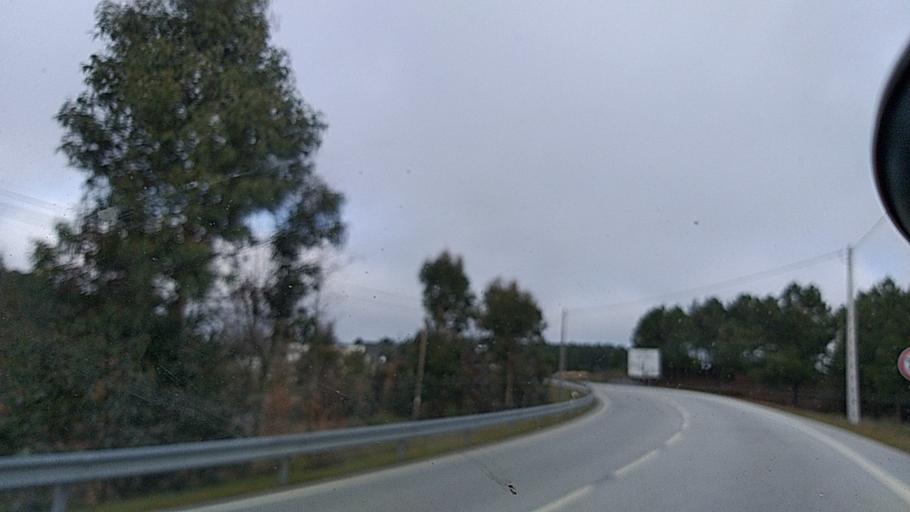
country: PT
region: Guarda
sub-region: Aguiar da Beira
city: Aguiar da Beira
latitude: 40.7865
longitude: -7.5023
